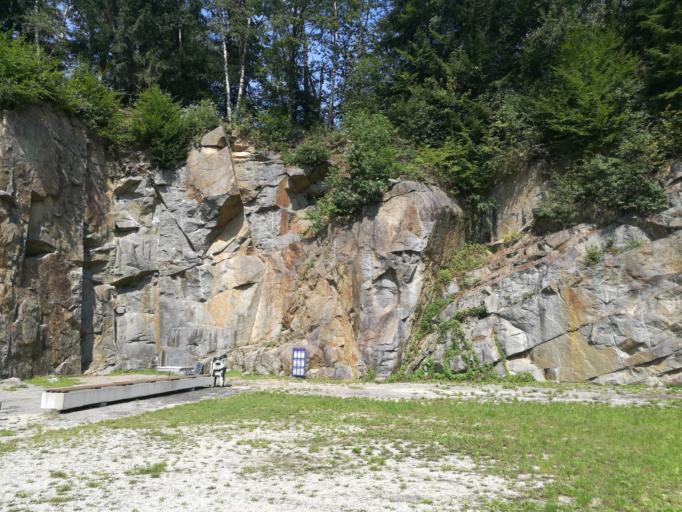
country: DE
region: Bavaria
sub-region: Lower Bavaria
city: Obernzell
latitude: 48.3733
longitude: 13.6560
